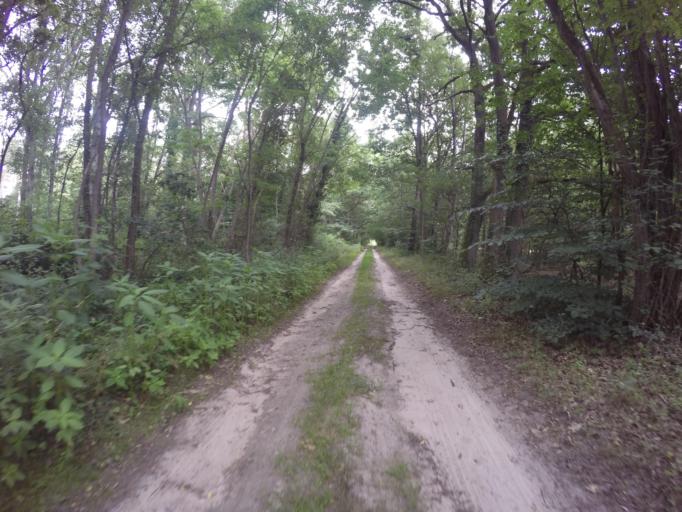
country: DE
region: Lower Saxony
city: Thomasburg
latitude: 53.2583
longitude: 10.6960
